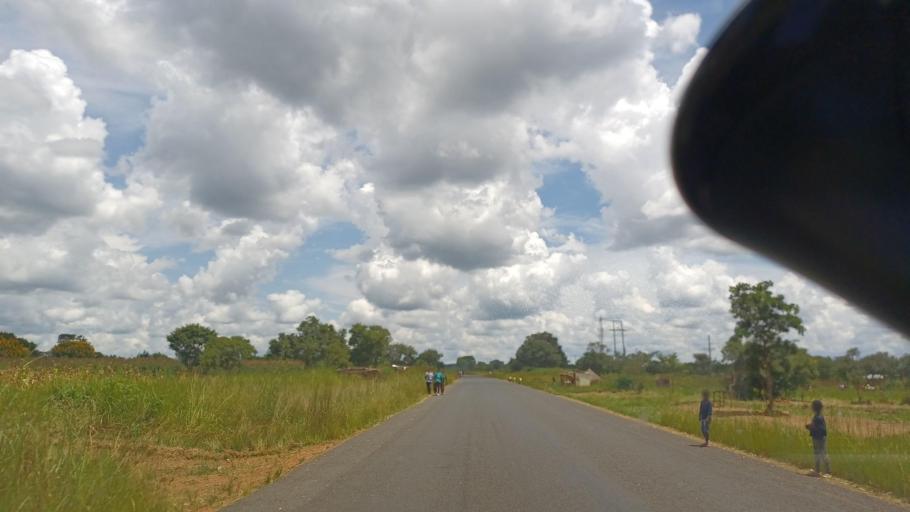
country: ZM
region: North-Western
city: Solwezi
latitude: -12.4179
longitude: 26.2268
